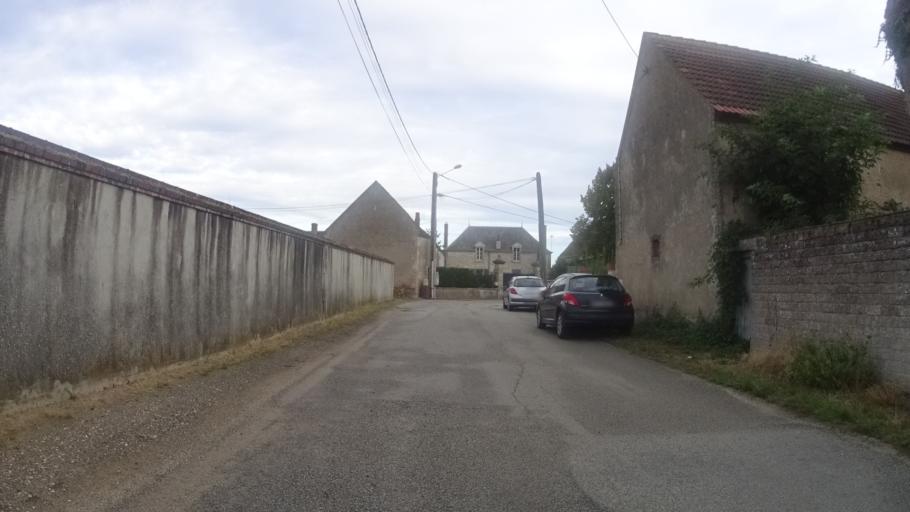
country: FR
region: Centre
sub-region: Departement du Loiret
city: Saint-Benoit-sur-Loire
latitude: 47.8023
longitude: 2.3129
